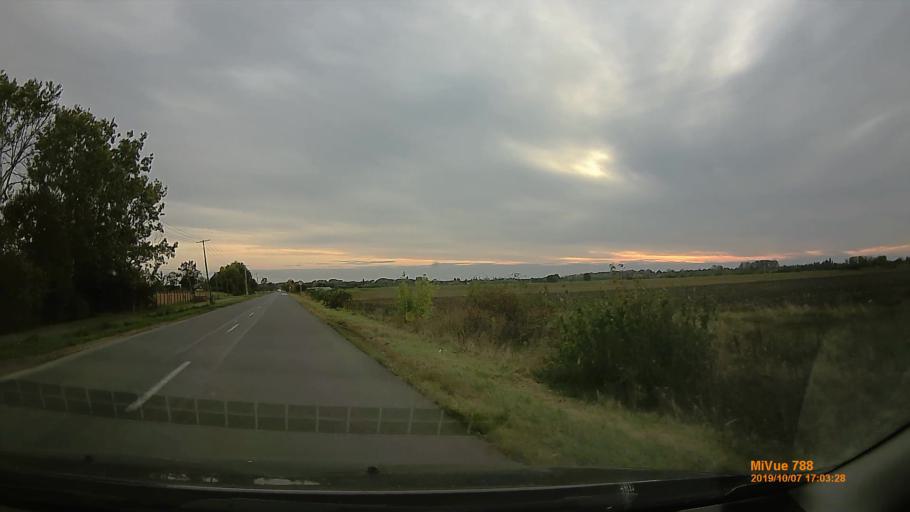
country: HU
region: Bekes
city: Szarvas
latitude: 46.8442
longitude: 20.5513
